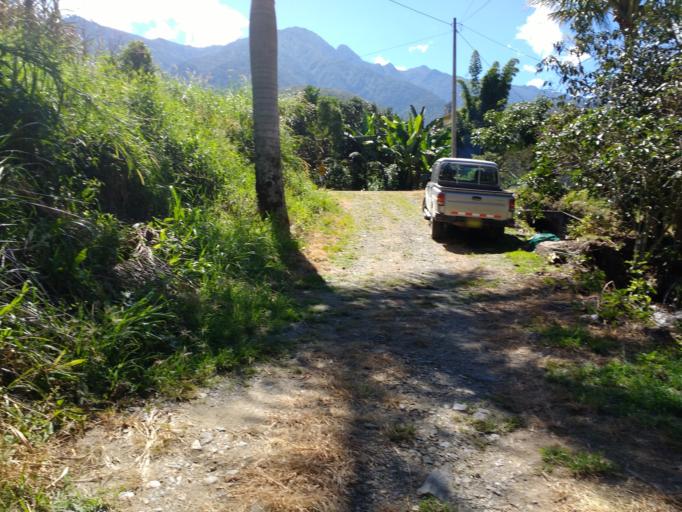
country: PE
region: Cusco
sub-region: Provincia de La Convencion
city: Maranura
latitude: -12.9996
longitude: -72.5324
